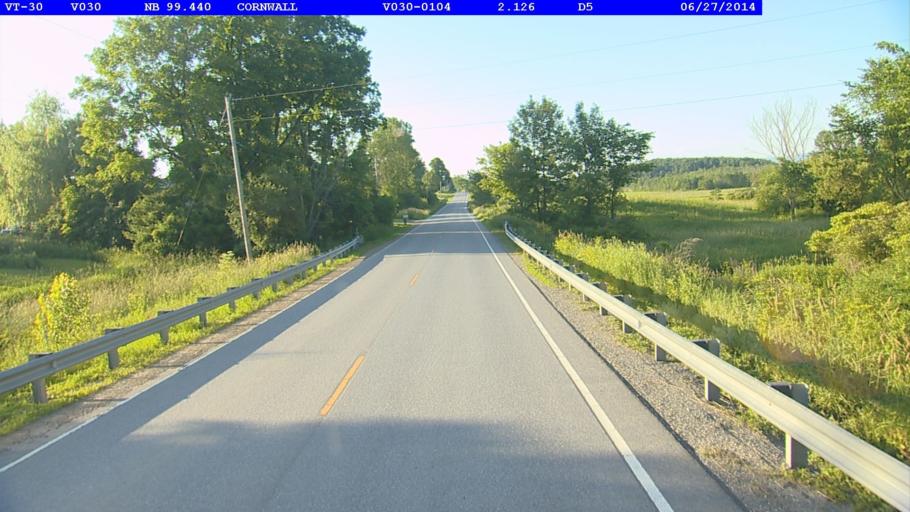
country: US
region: Vermont
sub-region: Addison County
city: Middlebury (village)
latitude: 43.9384
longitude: -73.2121
